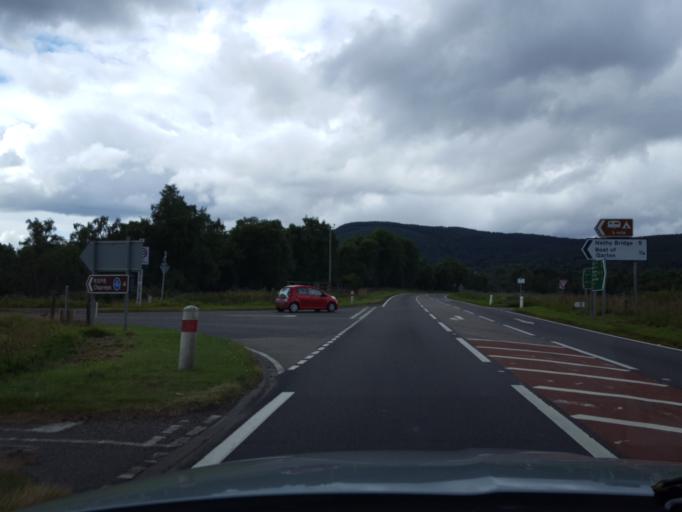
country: GB
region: Scotland
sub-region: Highland
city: Aviemore
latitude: 57.2511
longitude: -3.7845
